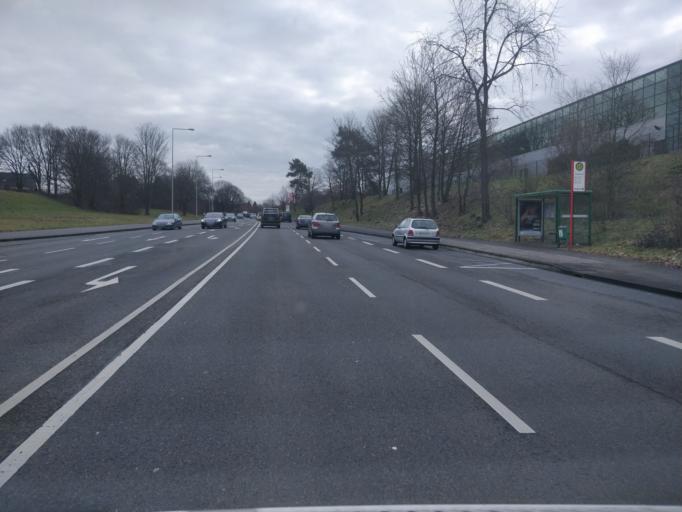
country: DE
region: North Rhine-Westphalia
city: Opladen
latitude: 51.0255
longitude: 7.0295
